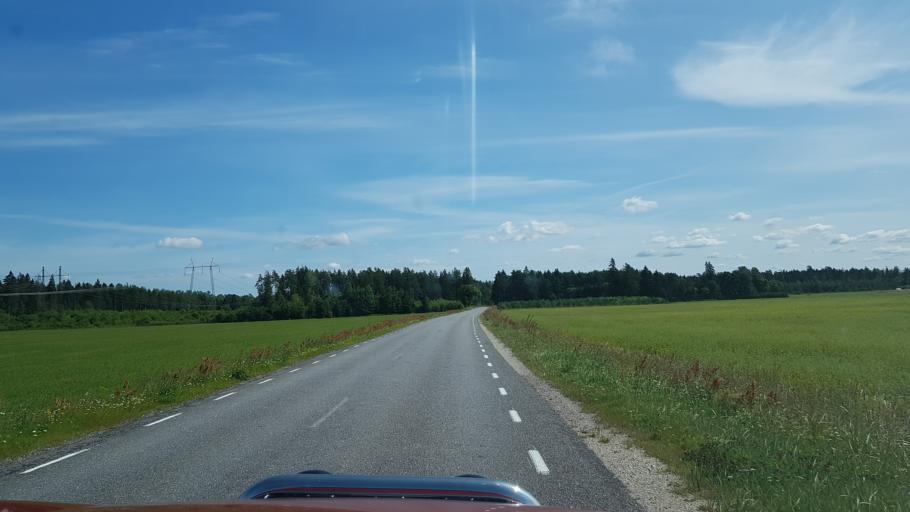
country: EE
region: Laeaene-Virumaa
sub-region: Tapa vald
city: Tapa
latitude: 59.1807
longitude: 25.9683
